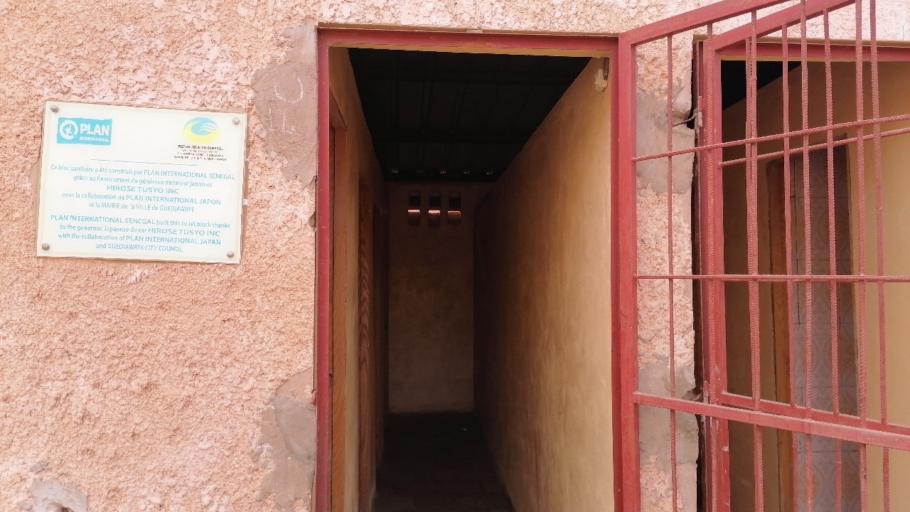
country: SN
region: Dakar
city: Pikine
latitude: 14.7806
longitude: -17.3825
